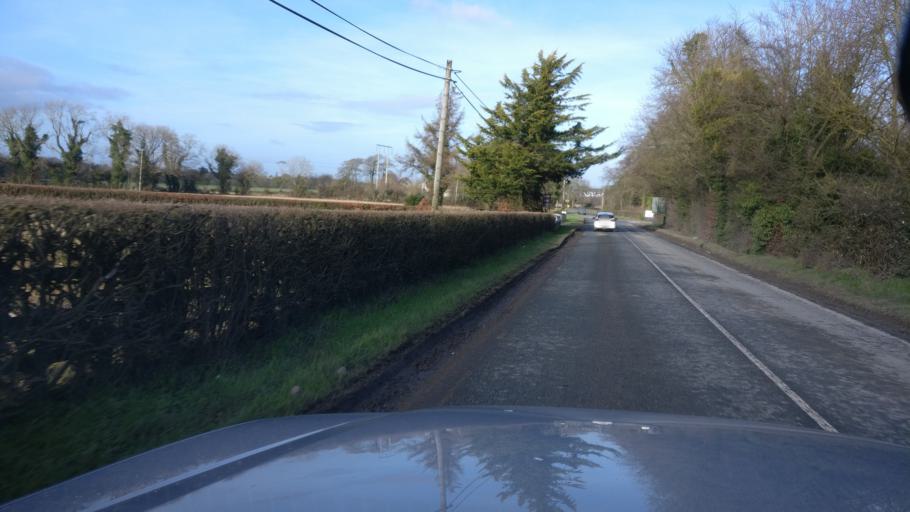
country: IE
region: Leinster
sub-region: Laois
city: Portlaoise
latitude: 53.0179
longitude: -7.2738
